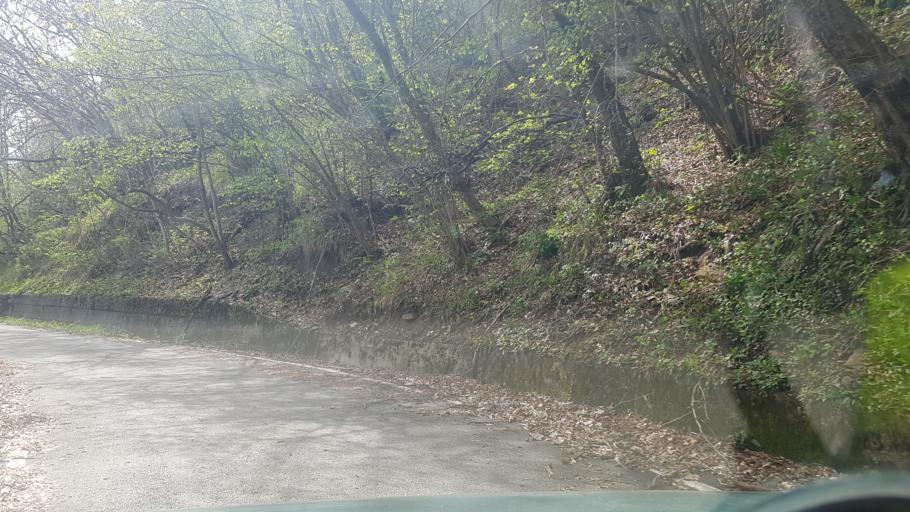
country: IT
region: Friuli Venezia Giulia
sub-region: Provincia di Udine
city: Faedis
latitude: 46.1850
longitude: 13.3778
